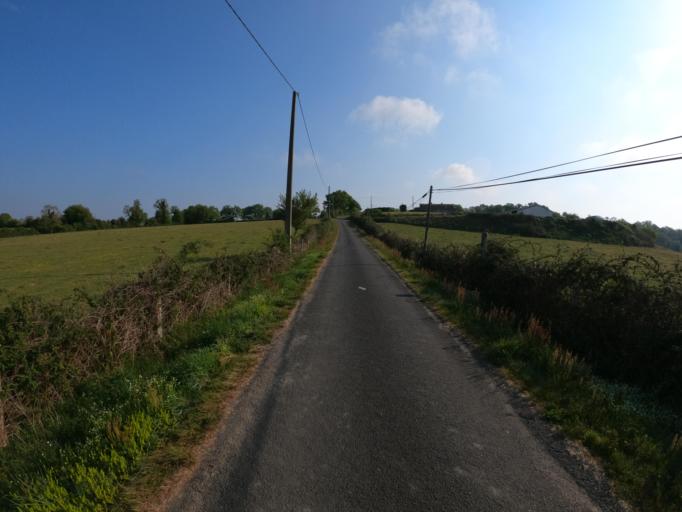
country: FR
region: Pays de la Loire
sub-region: Departement de Maine-et-Loire
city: La Romagne
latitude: 47.0692
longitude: -1.0072
